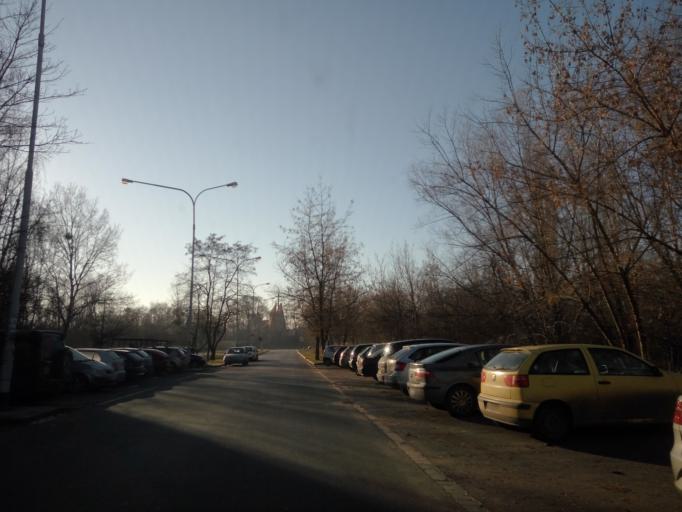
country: PL
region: Lower Silesian Voivodeship
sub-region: Powiat wroclawski
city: Wroclaw
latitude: 51.1275
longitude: 16.9567
